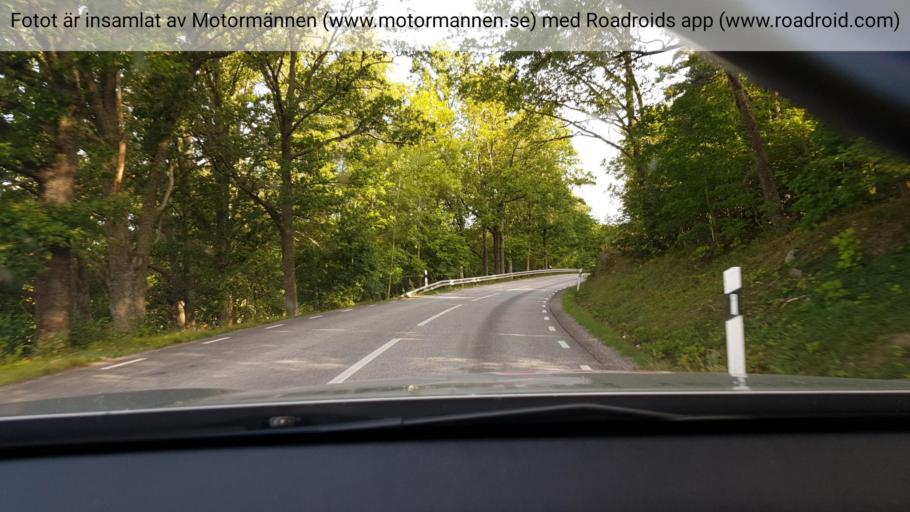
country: SE
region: Stockholm
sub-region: Norrtalje Kommun
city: Rimbo
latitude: 59.6927
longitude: 18.3694
